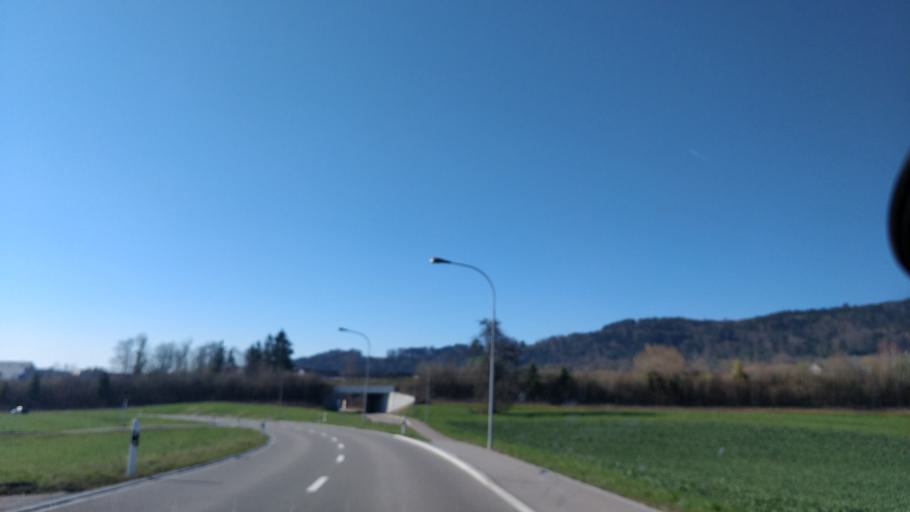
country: CH
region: Zurich
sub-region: Bezirk Uster
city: Hinteregg
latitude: 47.3096
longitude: 8.6887
